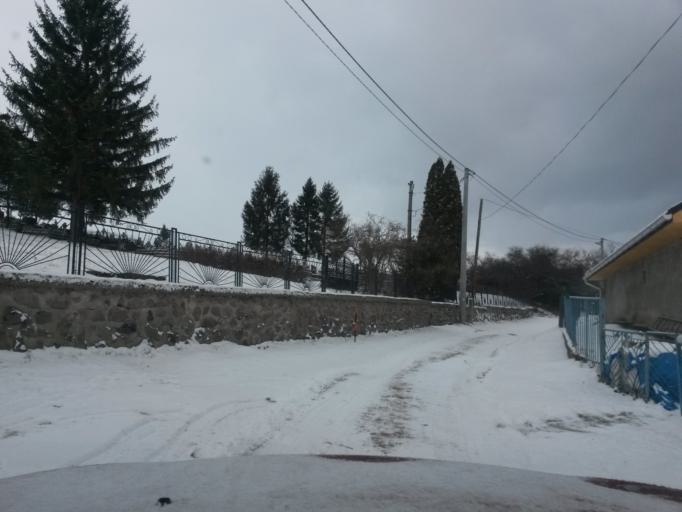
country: HU
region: Borsod-Abauj-Zemplen
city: Gonc
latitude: 48.5923
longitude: 21.3789
